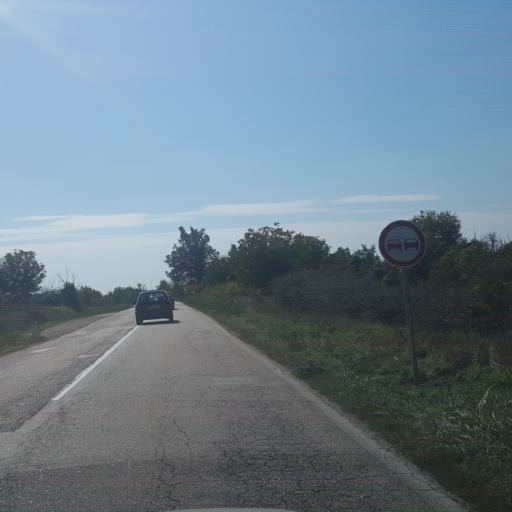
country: RS
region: Central Serbia
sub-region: Zajecarski Okrug
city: Zajecar
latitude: 43.7394
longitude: 22.3113
